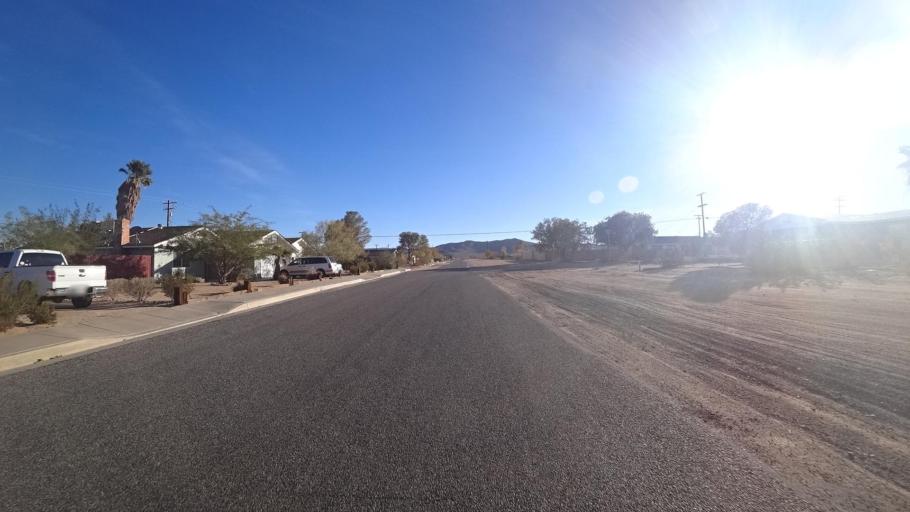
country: US
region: California
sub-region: Kern County
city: Ridgecrest
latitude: 35.5994
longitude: -117.6969
